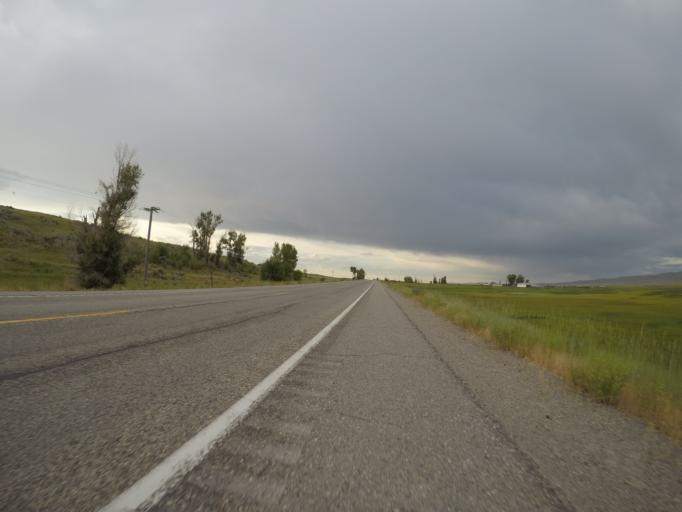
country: US
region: Idaho
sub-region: Bear Lake County
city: Montpelier
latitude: 42.0527
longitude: -110.9314
